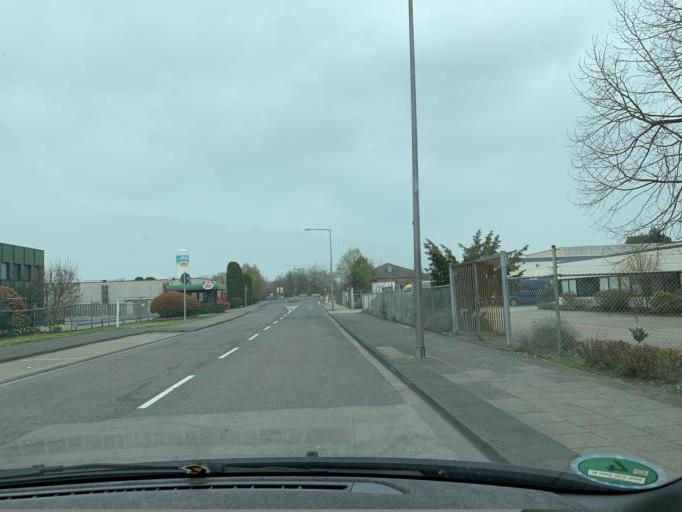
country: DE
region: North Rhine-Westphalia
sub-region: Regierungsbezirk Koln
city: Leverkusen
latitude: 51.0352
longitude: 6.9268
